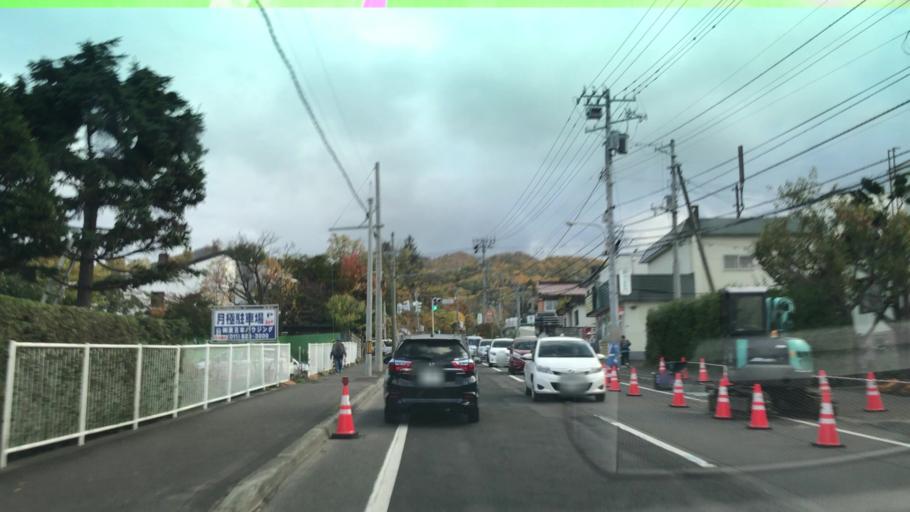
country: JP
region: Hokkaido
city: Sapporo
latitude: 43.0443
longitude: 141.3059
